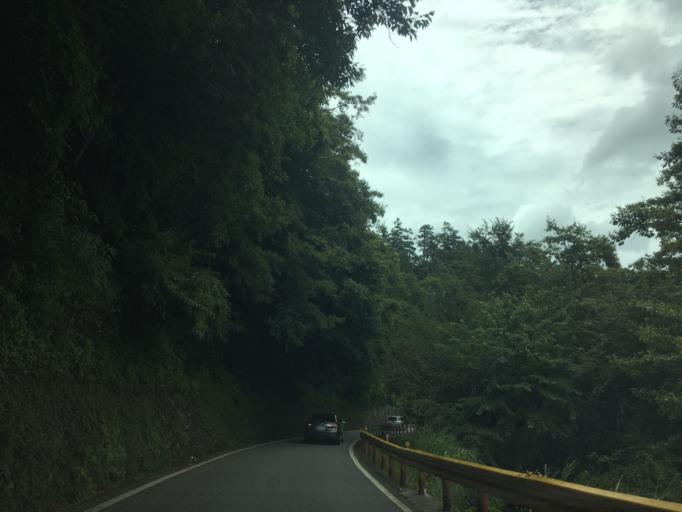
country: TW
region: Taiwan
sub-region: Hualien
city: Hualian
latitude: 24.1741
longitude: 121.3811
